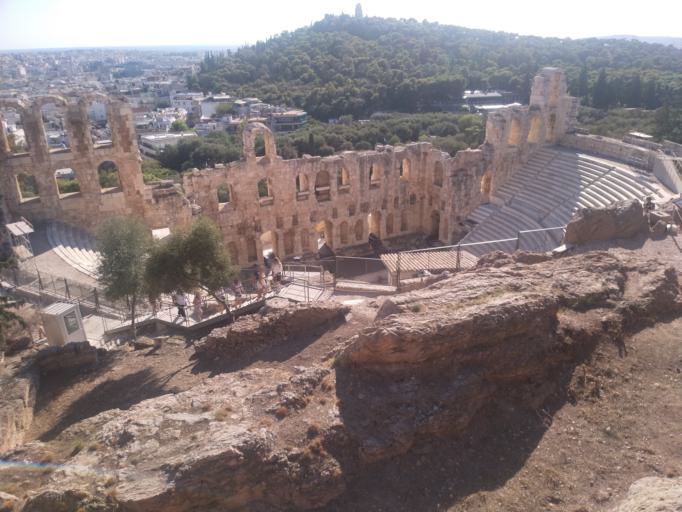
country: GR
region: Attica
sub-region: Nomarchia Athinas
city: Athens
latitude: 37.9692
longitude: 23.7227
